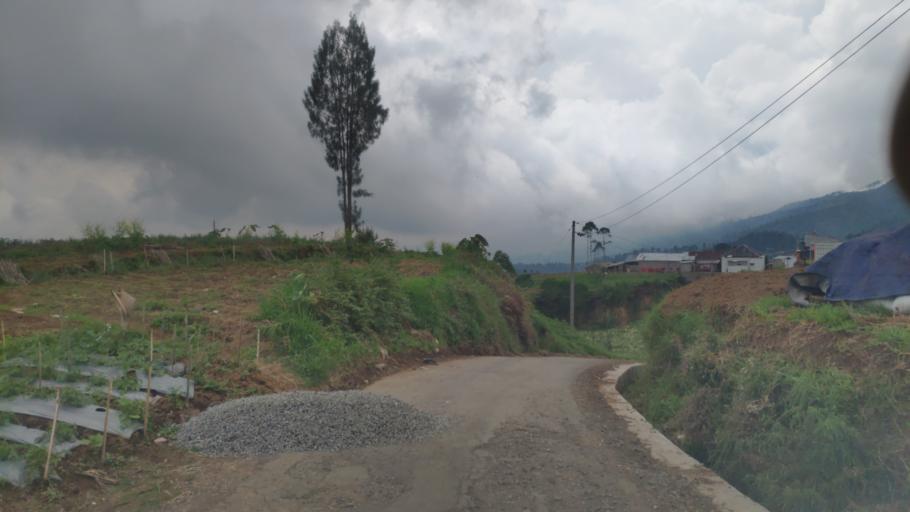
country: ID
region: Central Java
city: Wonosobo
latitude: -7.1914
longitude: 109.8082
